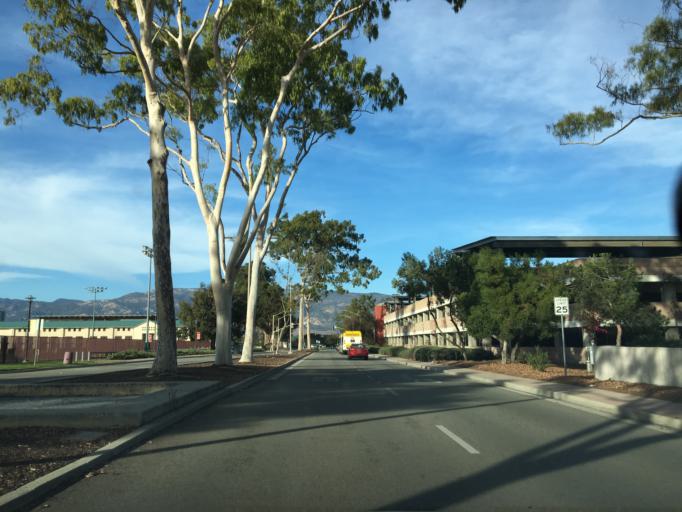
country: US
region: California
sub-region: Santa Barbara County
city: Isla Vista
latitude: 34.4165
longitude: -119.8482
